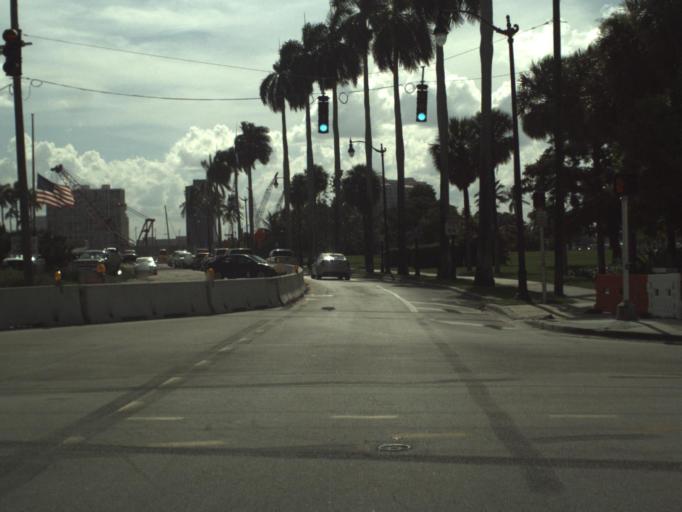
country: US
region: Florida
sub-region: Palm Beach County
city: West Palm Beach
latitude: 26.7185
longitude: -80.0410
